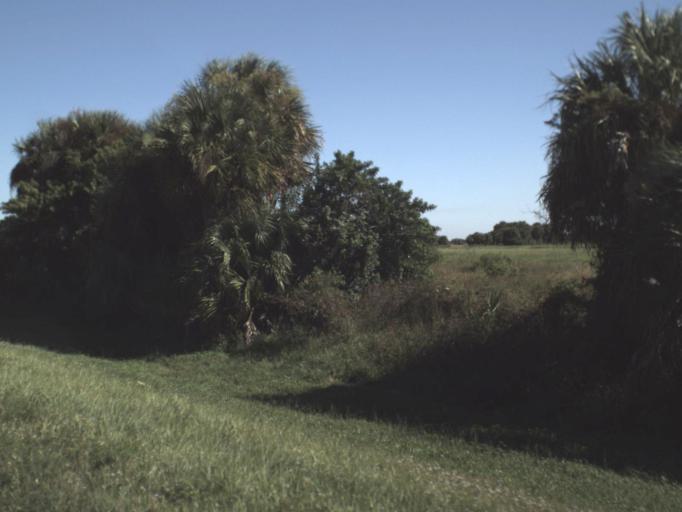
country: US
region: Florida
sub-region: Hendry County
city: Port LaBelle
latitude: 26.7685
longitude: -81.2901
